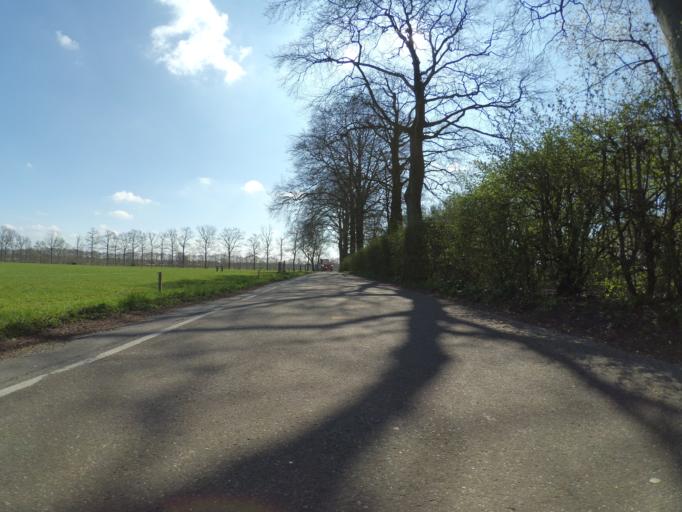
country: NL
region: Utrecht
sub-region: Gemeente Utrechtse Heuvelrug
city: Driebergen-Rijsenburg
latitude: 52.0318
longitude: 5.2885
